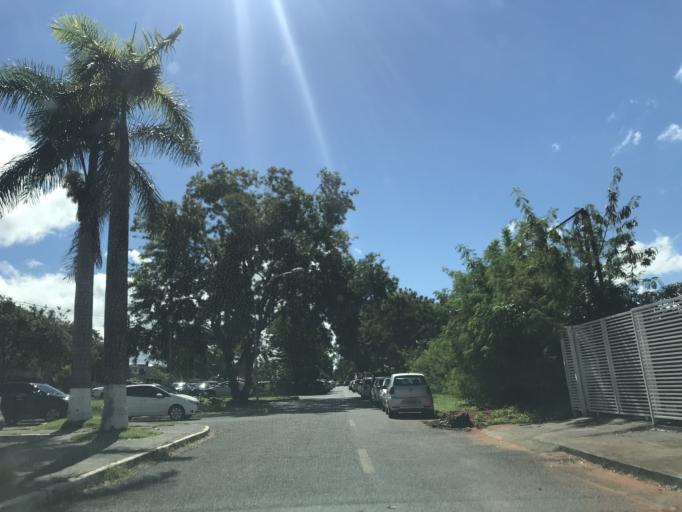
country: BR
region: Federal District
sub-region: Brasilia
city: Brasilia
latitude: -15.8222
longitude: -47.8959
